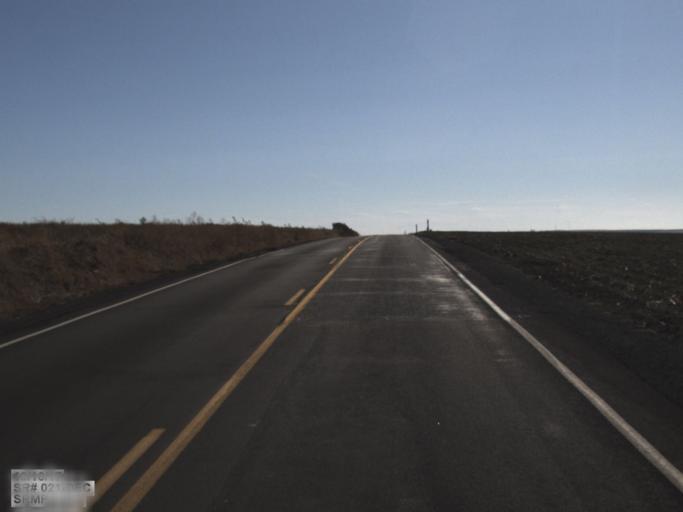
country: US
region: Washington
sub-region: Adams County
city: Ritzville
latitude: 47.0133
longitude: -118.6637
